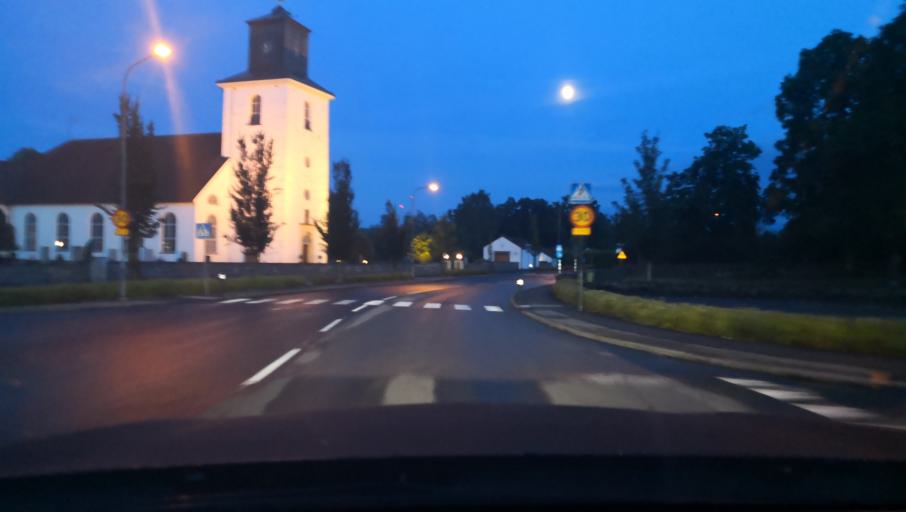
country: SE
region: Skane
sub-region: Osby Kommun
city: Osby
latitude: 56.3815
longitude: 14.0003
